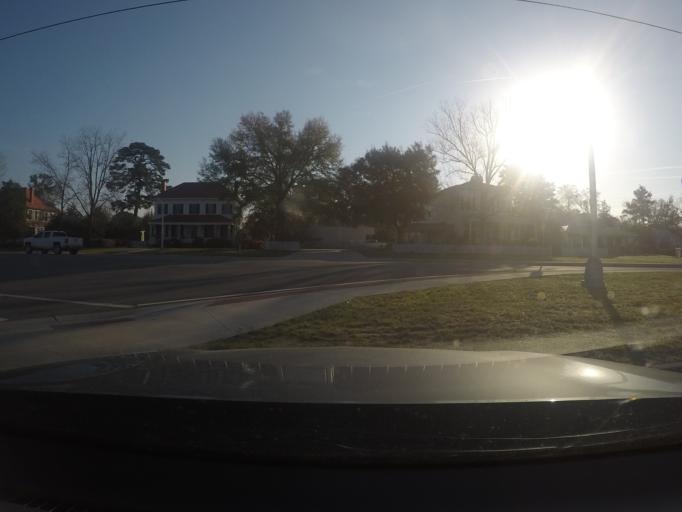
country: US
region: Georgia
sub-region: Effingham County
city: Guyton
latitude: 32.3308
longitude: -81.3932
